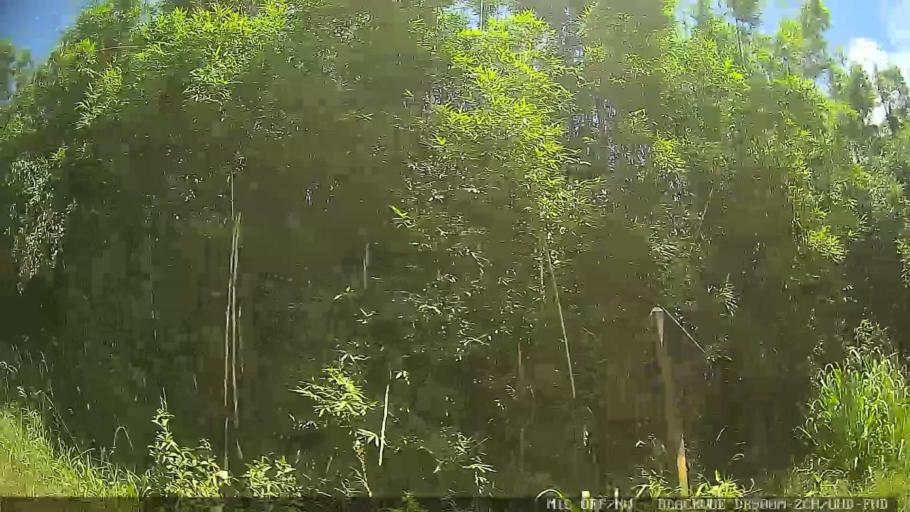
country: BR
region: Sao Paulo
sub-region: Biritiba-Mirim
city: Biritiba Mirim
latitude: -23.5832
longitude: -46.0819
